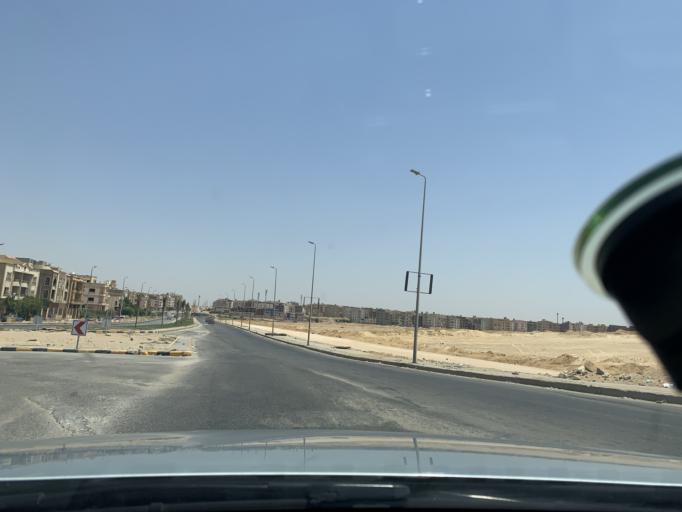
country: EG
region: Muhafazat al Qahirah
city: Cairo
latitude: 29.9994
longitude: 31.4631
